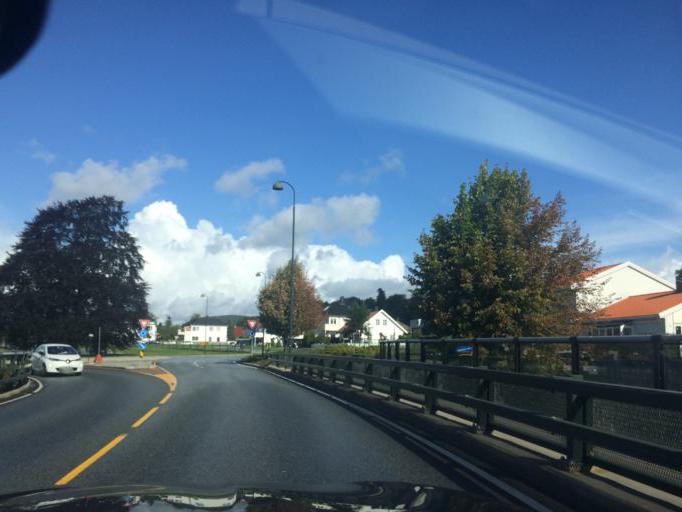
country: NO
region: Vest-Agder
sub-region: Kristiansand
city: Kristiansand
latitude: 58.1545
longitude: 8.0042
